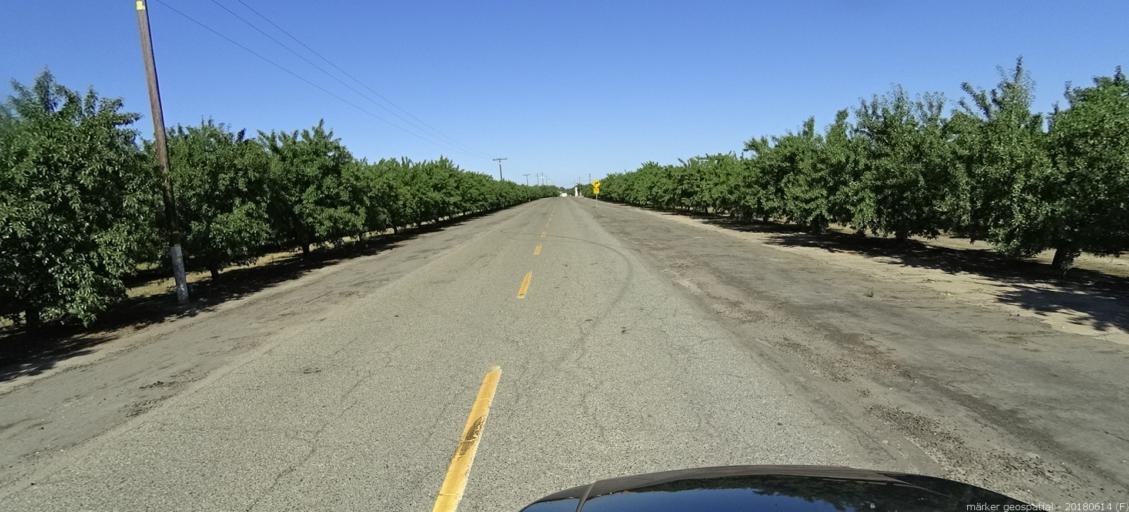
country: US
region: California
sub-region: Madera County
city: Fairmead
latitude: 36.9819
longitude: -120.1631
